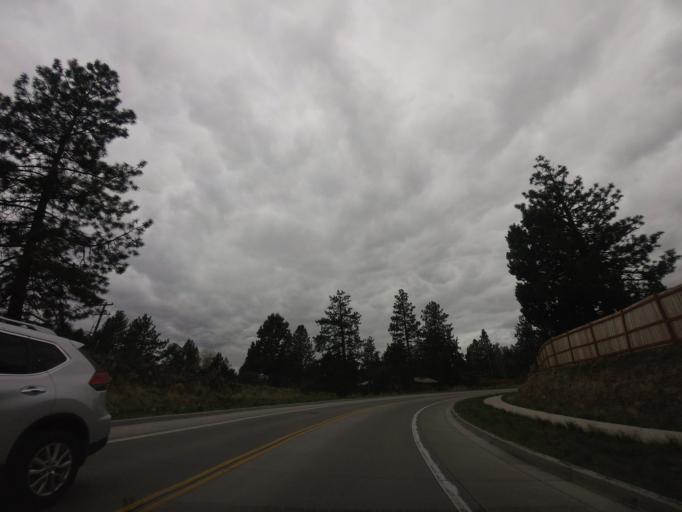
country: US
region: Oregon
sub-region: Deschutes County
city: Bend
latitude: 44.0193
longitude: -121.3272
